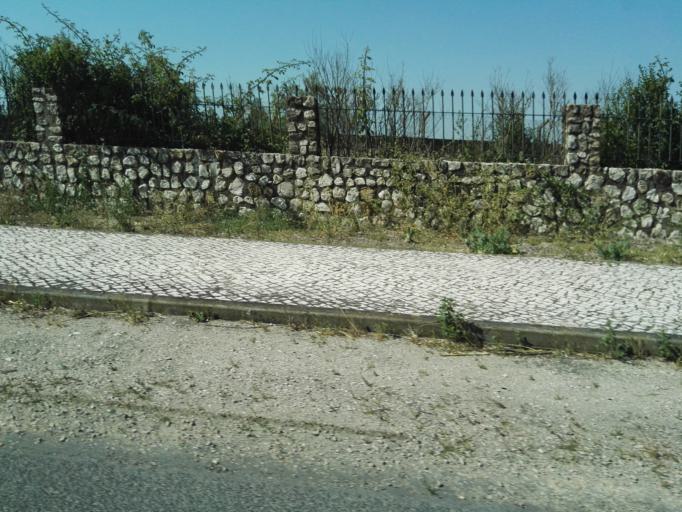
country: PT
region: Santarem
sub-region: Benavente
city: Samora Correia
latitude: 38.9369
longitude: -8.8609
